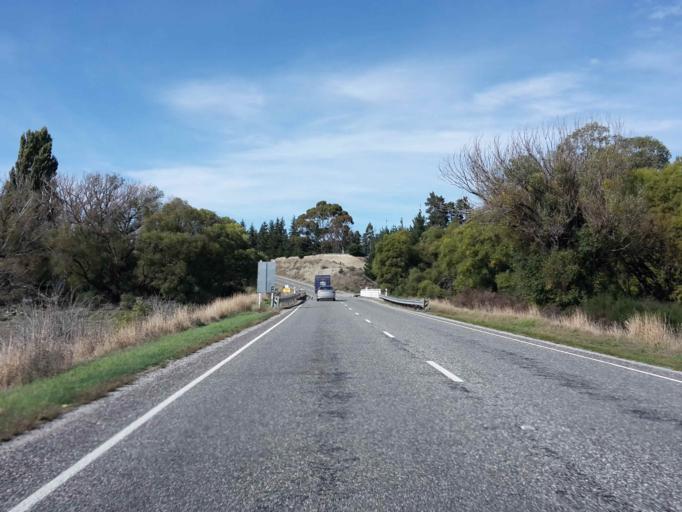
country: NZ
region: Otago
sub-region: Queenstown-Lakes District
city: Wanaka
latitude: -44.6983
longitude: 169.1765
